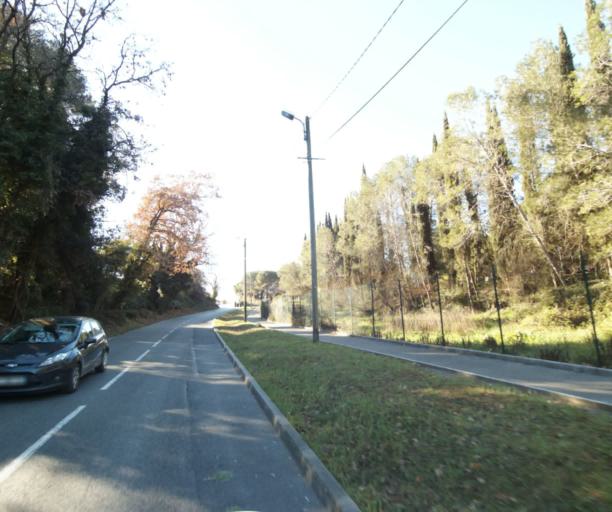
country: FR
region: Provence-Alpes-Cote d'Azur
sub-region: Departement des Alpes-Maritimes
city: Vallauris
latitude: 43.5997
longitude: 7.0759
